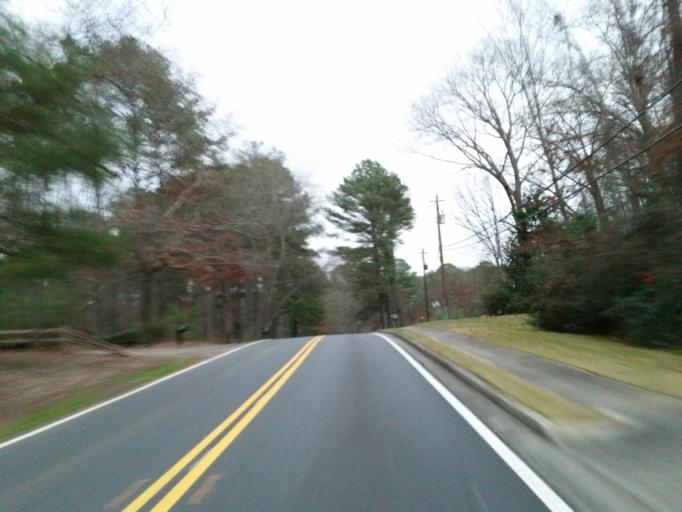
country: US
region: Georgia
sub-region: Cobb County
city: Mableton
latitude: 33.8460
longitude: -84.5705
